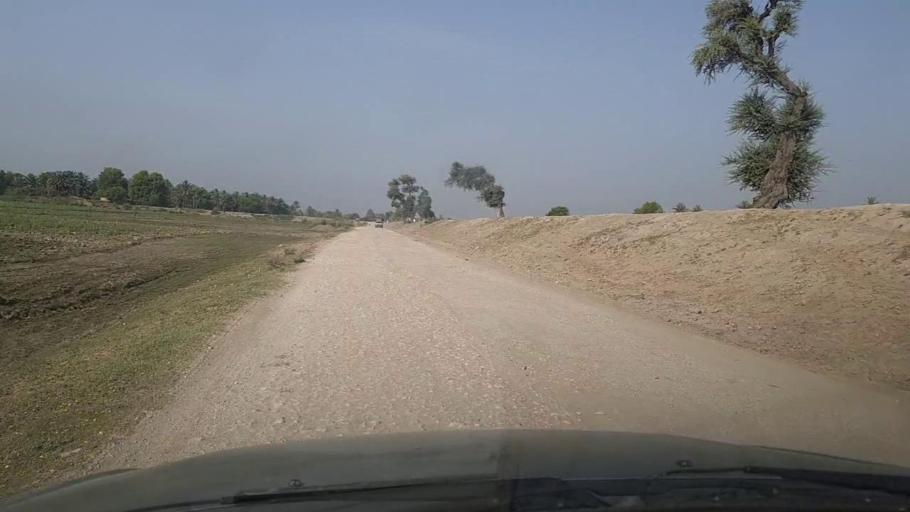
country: PK
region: Sindh
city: Pir jo Goth
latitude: 27.5342
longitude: 68.5101
